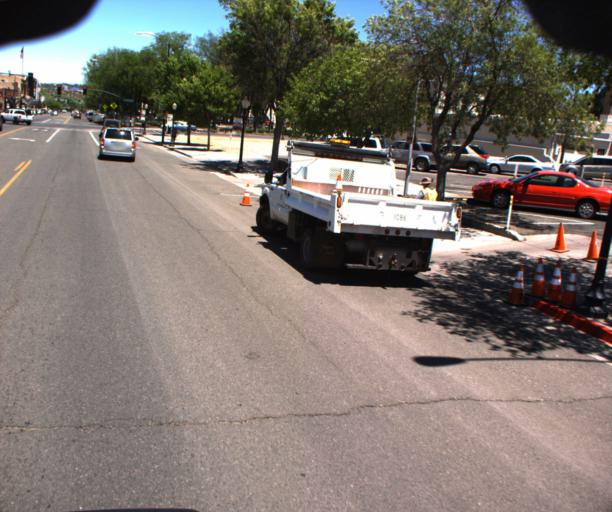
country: US
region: Arizona
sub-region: Yavapai County
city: Prescott
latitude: 34.5391
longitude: -112.4701
